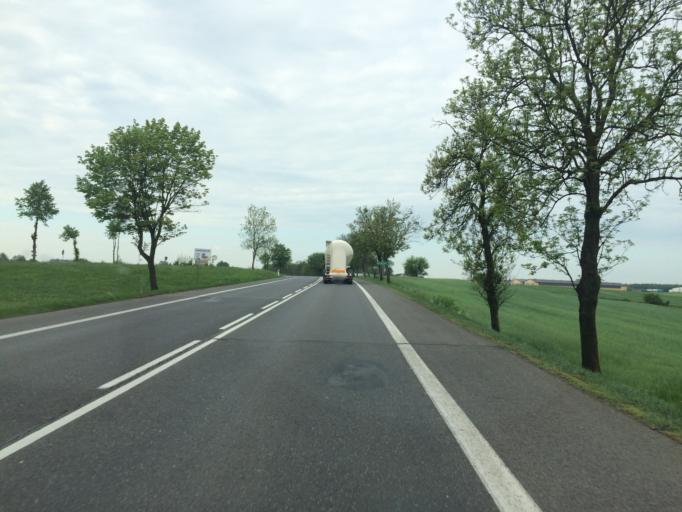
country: PL
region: Masovian Voivodeship
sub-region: Powiat mlawski
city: Wisniewo
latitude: 53.0821
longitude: 20.3565
